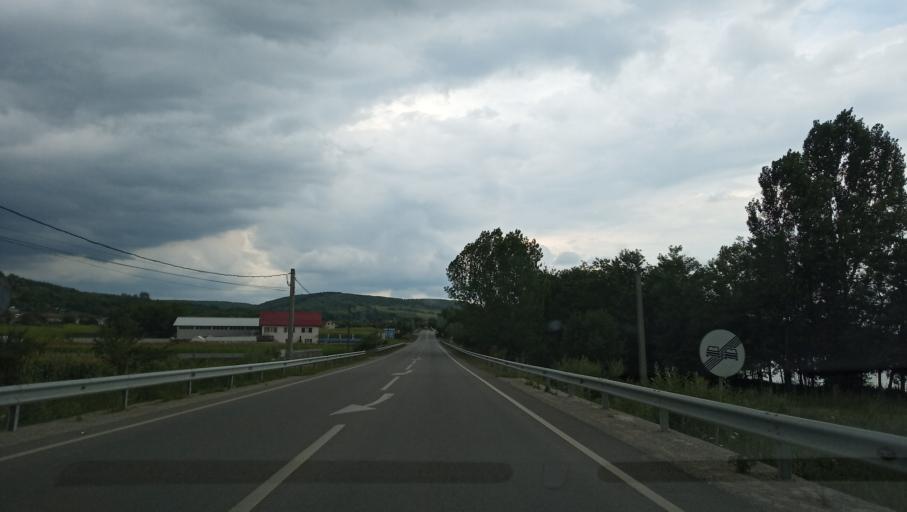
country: RO
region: Gorj
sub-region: Oras Rovinari
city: Rovinari
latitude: 44.9009
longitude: 23.1963
